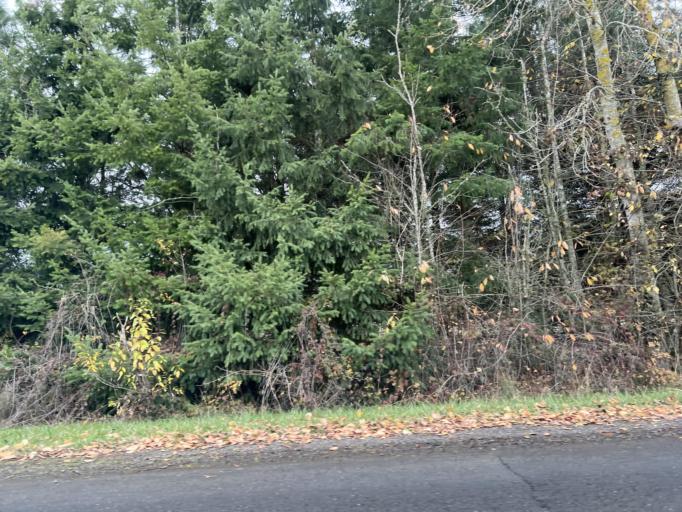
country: US
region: Oregon
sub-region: Polk County
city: Independence
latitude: 44.8078
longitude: -123.0849
